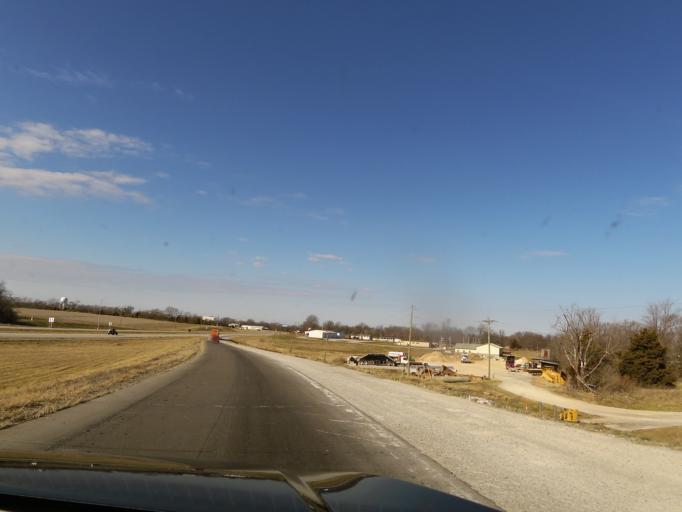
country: US
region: Missouri
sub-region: Ralls County
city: New London
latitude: 39.5749
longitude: -91.4000
